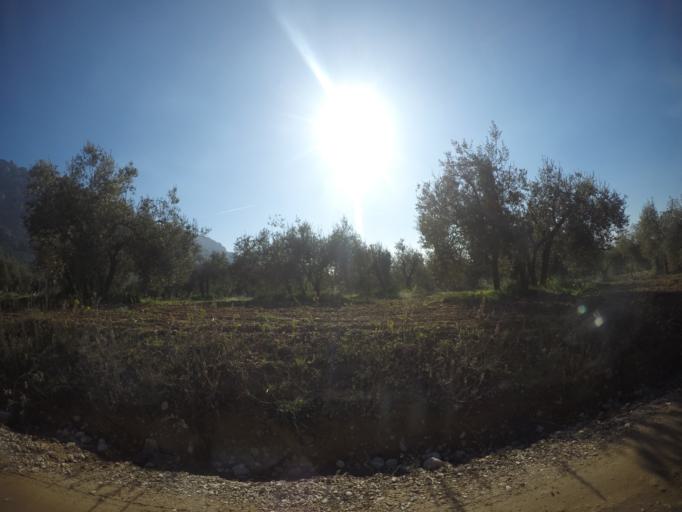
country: ES
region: Catalonia
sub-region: Provincia de Barcelona
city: Collbato
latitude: 41.5815
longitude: 1.8065
